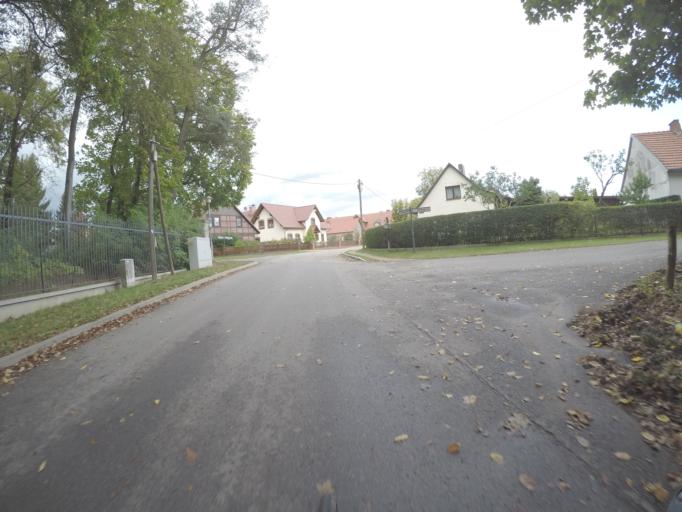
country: DE
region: Brandenburg
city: Strausberg
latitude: 52.6092
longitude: 13.9041
